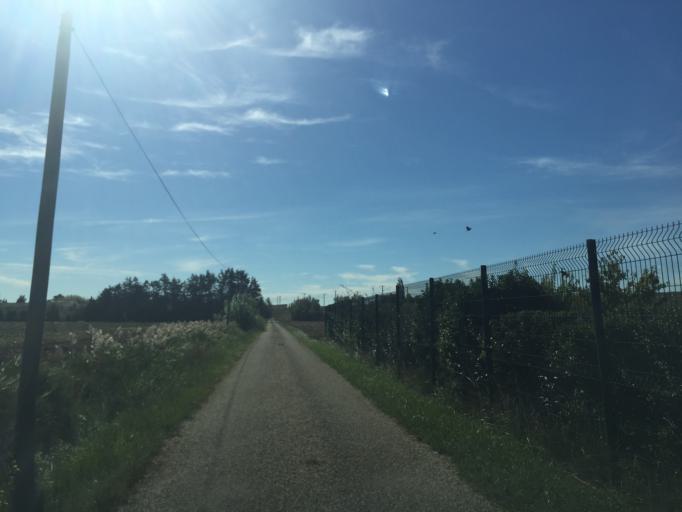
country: FR
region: Provence-Alpes-Cote d'Azur
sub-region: Departement du Vaucluse
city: Caderousse
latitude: 44.1349
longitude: 4.7671
